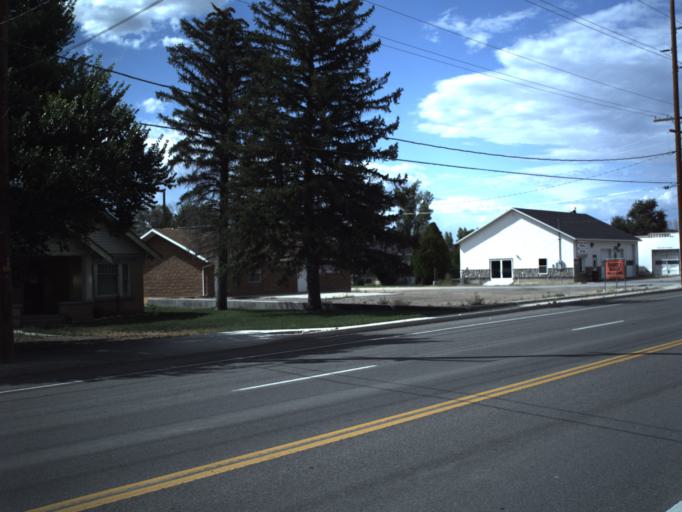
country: US
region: Utah
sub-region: Sanpete County
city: Centerfield
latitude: 39.1241
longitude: -111.8192
